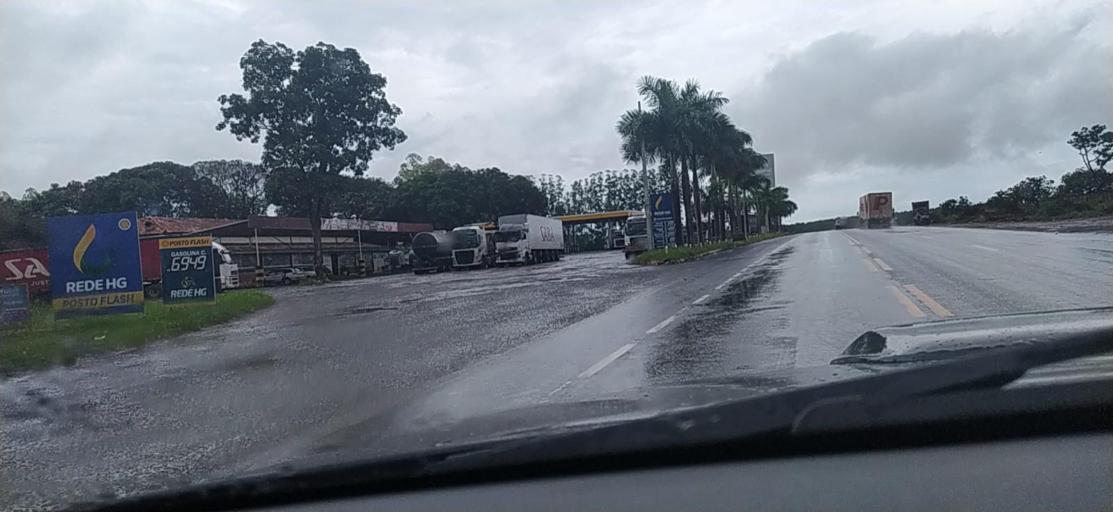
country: BR
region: Minas Gerais
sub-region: Curvelo
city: Curvelo
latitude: -18.9405
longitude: -44.4972
